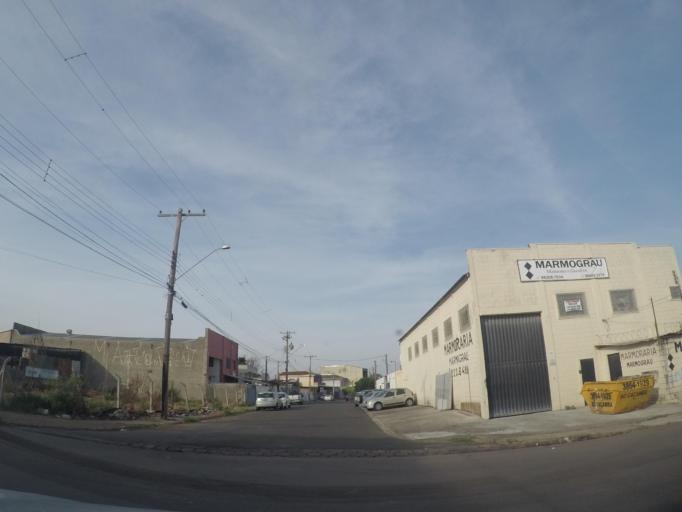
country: BR
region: Sao Paulo
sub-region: Hortolandia
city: Hortolandia
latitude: -22.8297
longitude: -47.1849
